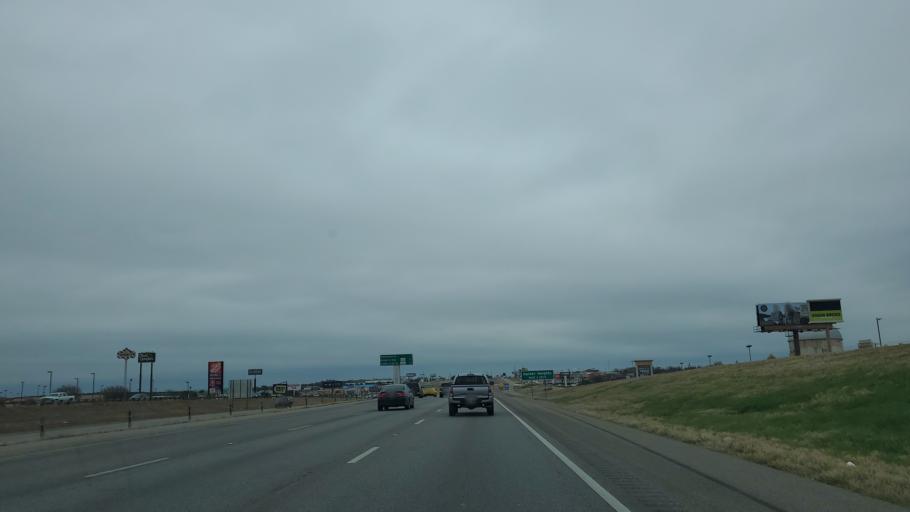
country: US
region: Texas
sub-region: Bell County
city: Killeen
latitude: 31.0869
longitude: -97.7121
